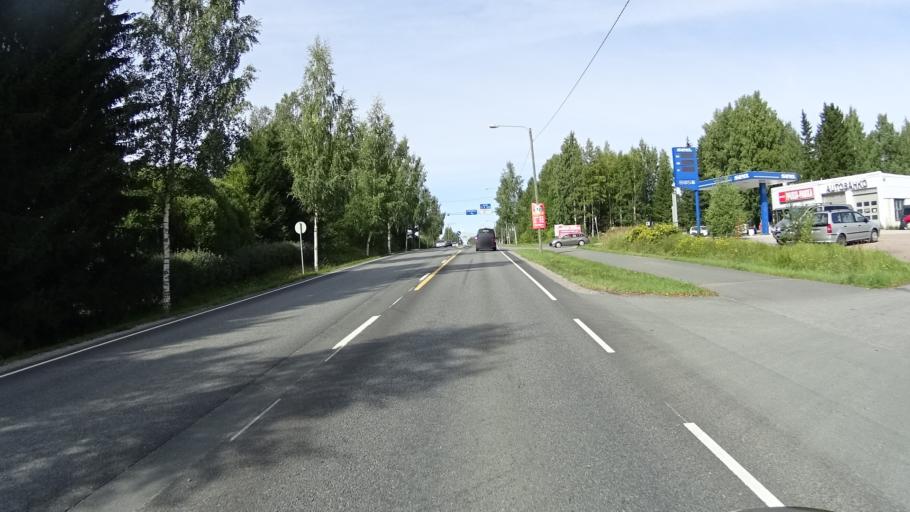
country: FI
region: Pirkanmaa
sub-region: Tampere
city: Haemeenkyroe
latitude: 61.6429
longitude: 23.1905
